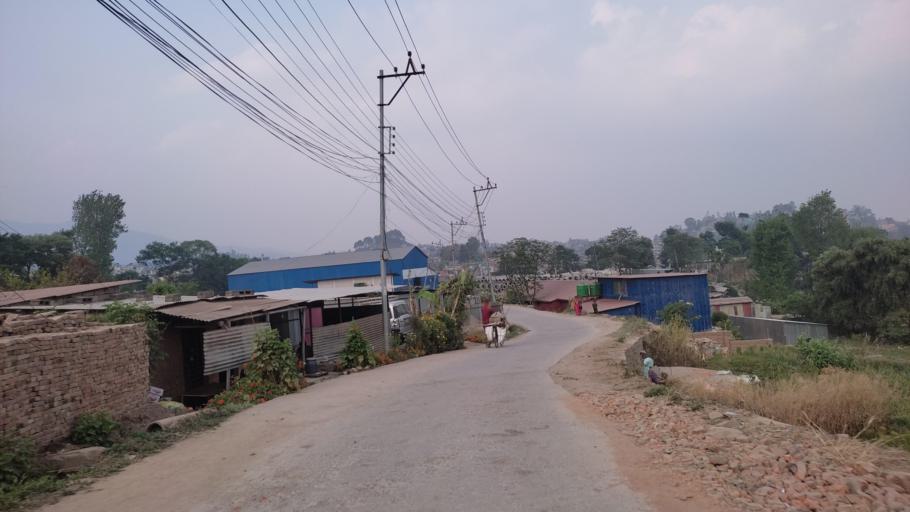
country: NP
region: Central Region
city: Kirtipur
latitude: 27.6797
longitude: 85.2529
